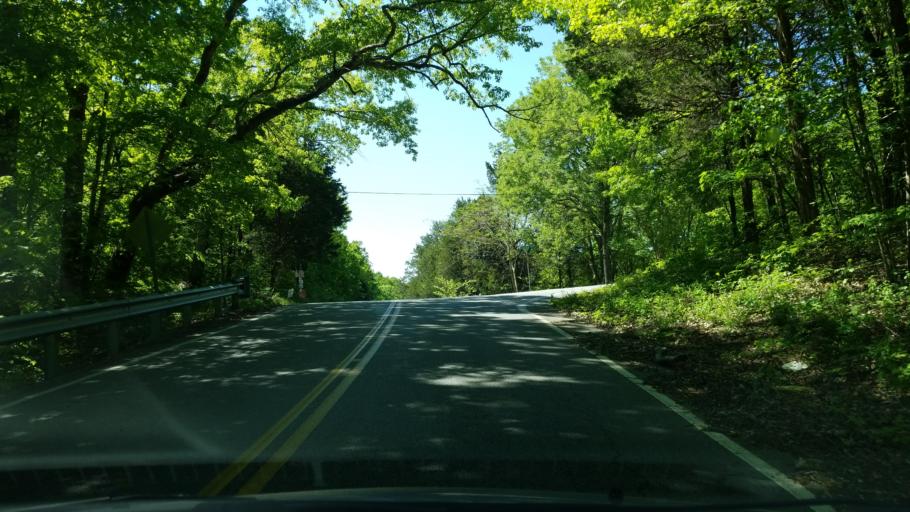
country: US
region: Tennessee
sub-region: Hamilton County
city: Middle Valley
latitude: 35.1691
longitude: -85.1749
